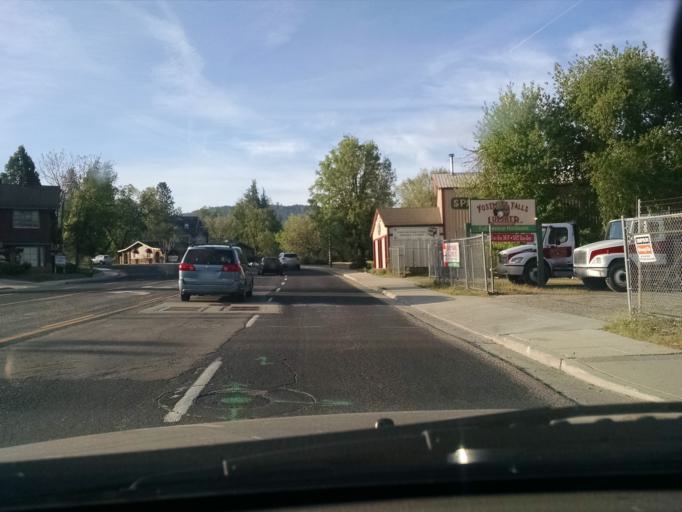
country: US
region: California
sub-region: Madera County
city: Oakhurst
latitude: 37.3301
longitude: -119.6507
